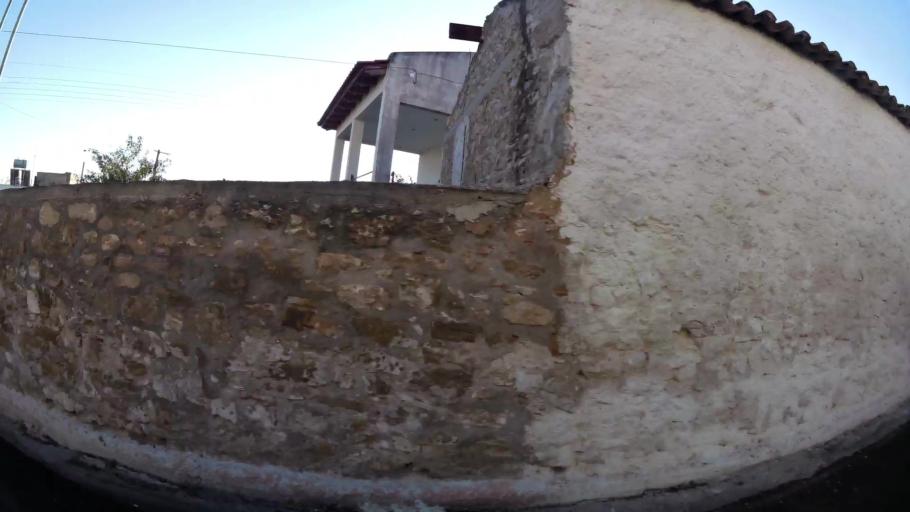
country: GR
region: Attica
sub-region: Nomarchia Anatolikis Attikis
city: Spata
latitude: 37.9593
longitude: 23.9140
